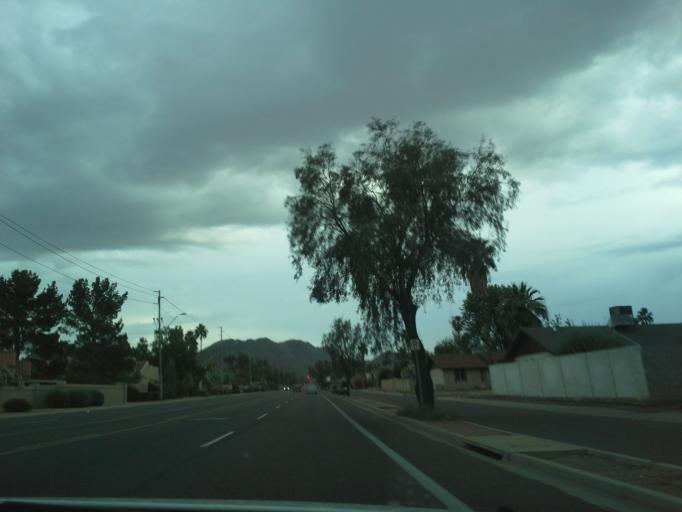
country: US
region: Arizona
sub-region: Maricopa County
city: Paradise Valley
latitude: 33.5940
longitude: -111.9959
